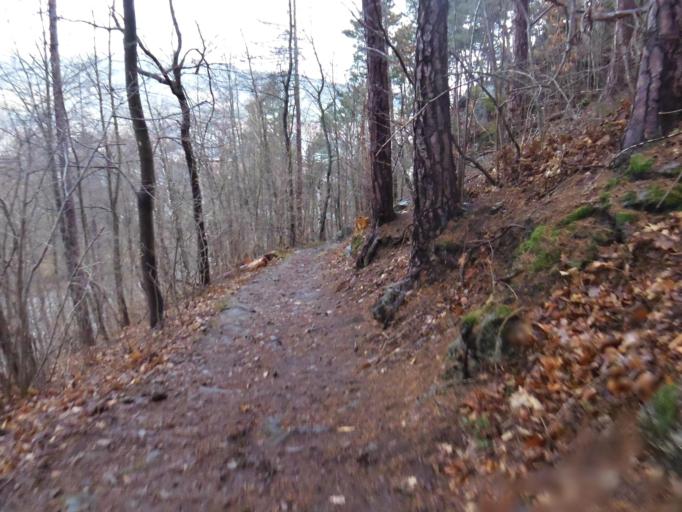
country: CZ
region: Plzensky
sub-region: Okres Klatovy
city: Susice
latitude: 49.2348
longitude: 13.5254
